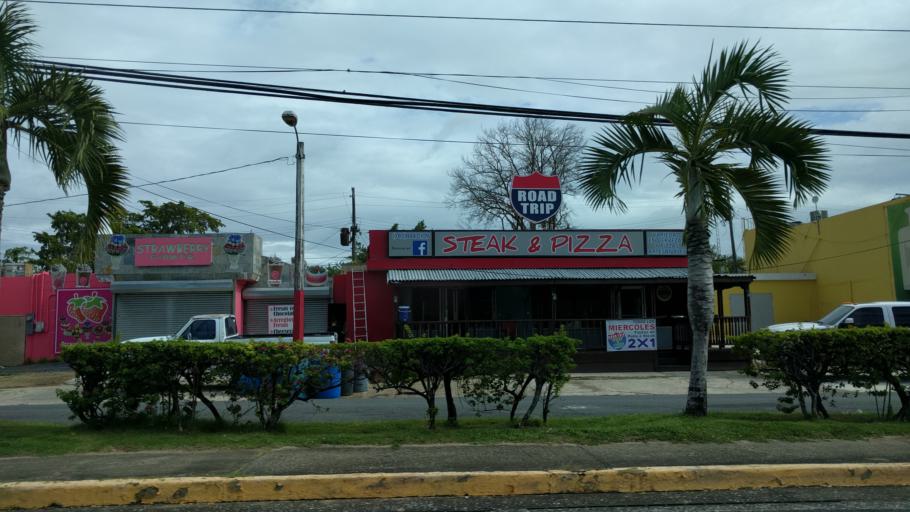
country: PR
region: Manati
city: Manati
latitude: 18.4324
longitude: -66.4871
